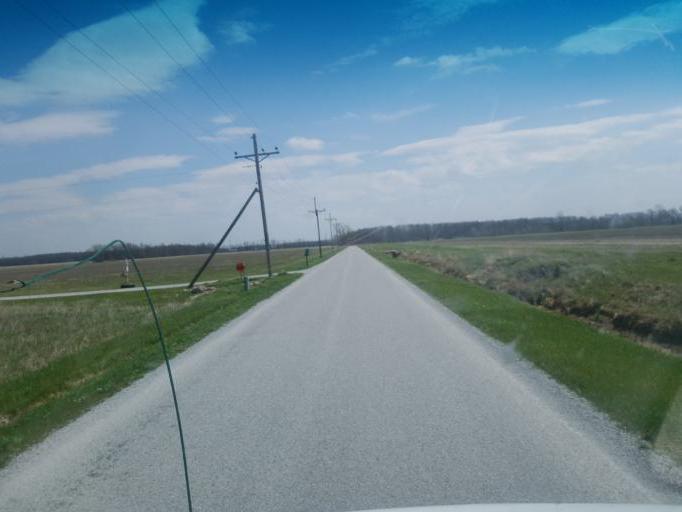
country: US
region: Ohio
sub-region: Hardin County
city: Forest
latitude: 40.7596
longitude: -83.5017
